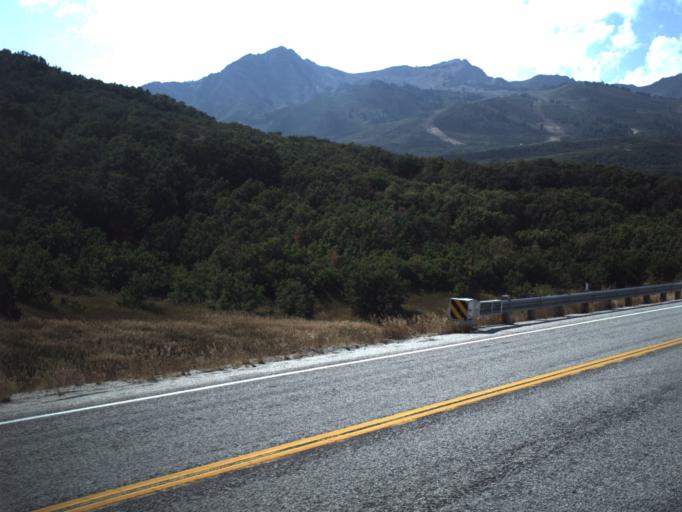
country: US
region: Utah
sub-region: Morgan County
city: Mountain Green
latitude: 41.1931
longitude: -111.8146
